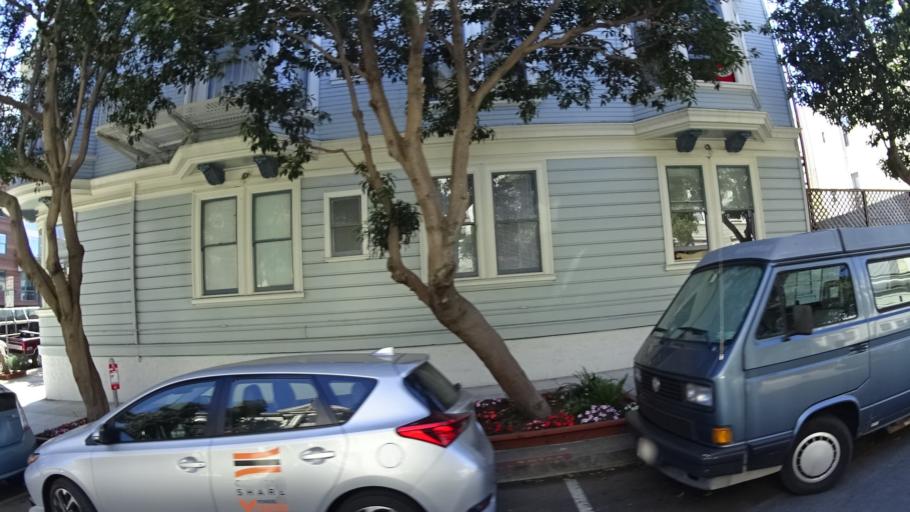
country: US
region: California
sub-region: San Francisco County
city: San Francisco
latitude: 37.7668
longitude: -122.4312
